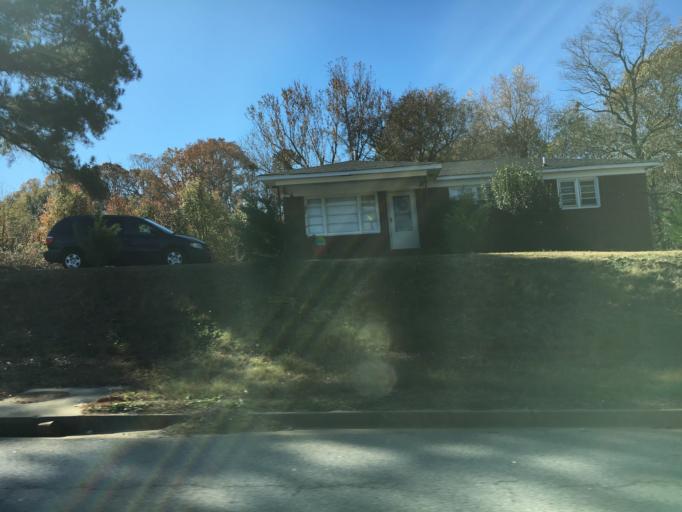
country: US
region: South Carolina
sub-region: Spartanburg County
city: Roebuck
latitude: 34.8464
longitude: -82.0066
